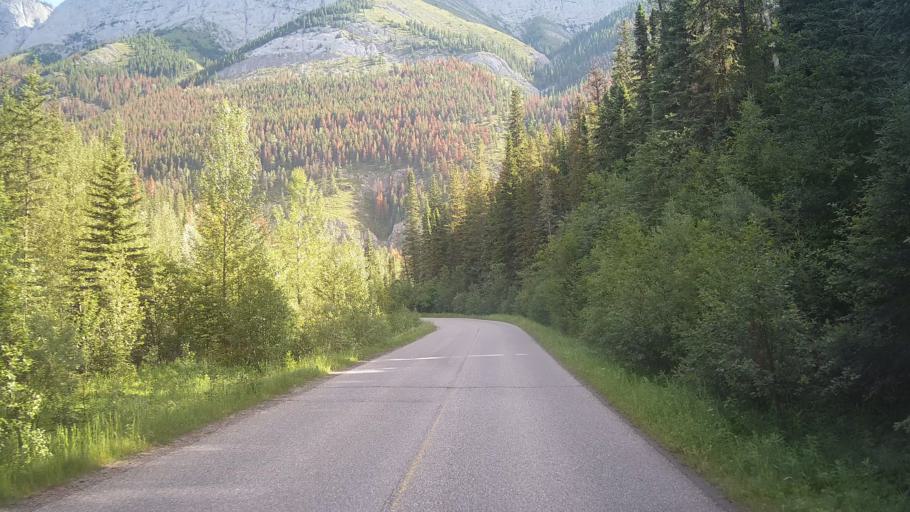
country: CA
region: Alberta
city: Hinton
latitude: 53.1766
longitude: -117.8389
